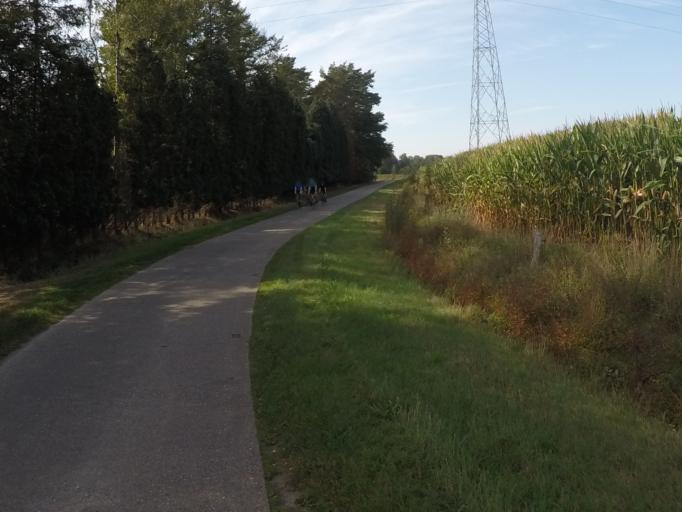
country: BE
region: Flanders
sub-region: Provincie Antwerpen
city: Lille
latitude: 51.2471
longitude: 4.8518
